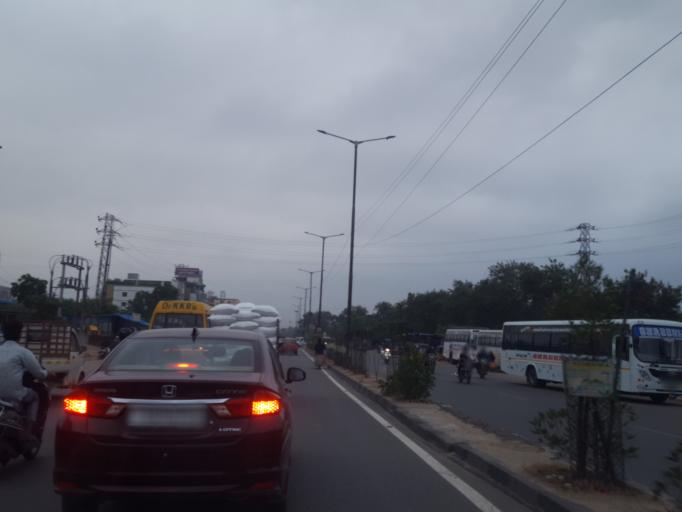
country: IN
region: Telangana
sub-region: Medak
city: Serilingampalle
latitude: 17.5009
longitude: 78.3126
